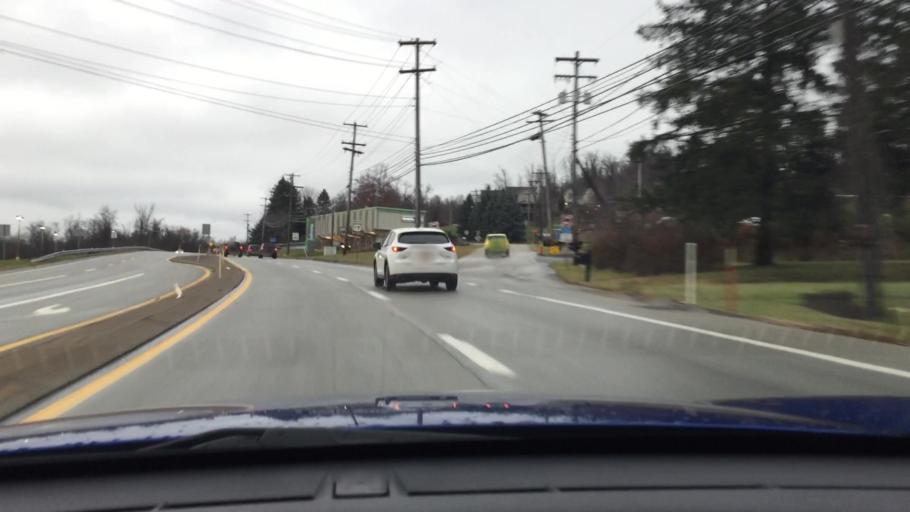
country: US
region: Pennsylvania
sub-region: Washington County
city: East Washington
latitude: 40.1906
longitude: -80.2128
